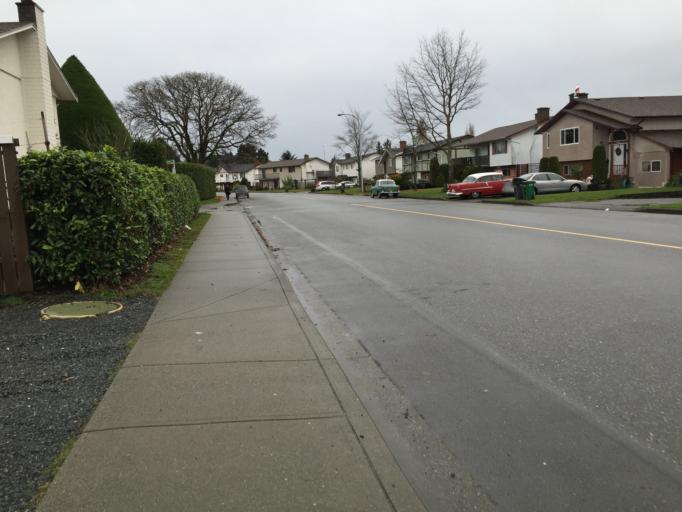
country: CA
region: British Columbia
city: Oak Bay
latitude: 48.4713
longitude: -123.3251
